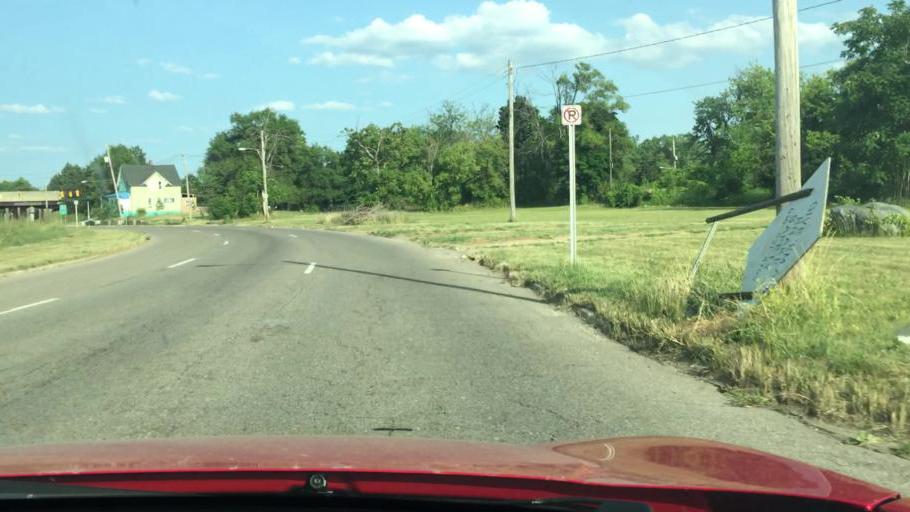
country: US
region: Michigan
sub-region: Genesee County
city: Flint
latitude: 43.0334
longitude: -83.6798
